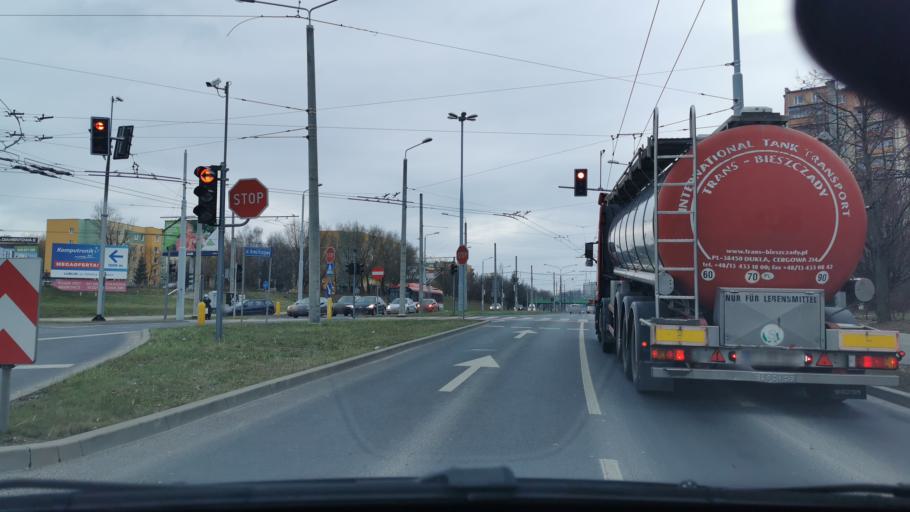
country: PL
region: Lublin Voivodeship
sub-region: Powiat lubelski
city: Lublin
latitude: 51.2318
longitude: 22.5126
